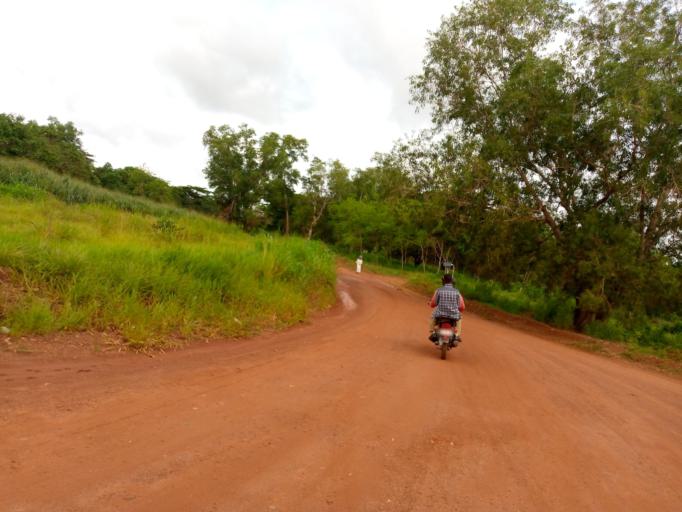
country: SL
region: Southern Province
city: Mogbwemo
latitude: 7.7664
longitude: -12.2975
